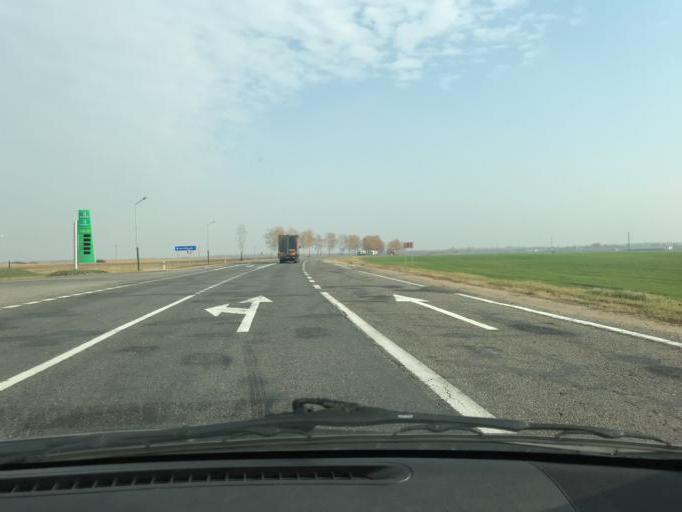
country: BY
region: Vitebsk
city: Chashniki
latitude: 55.0162
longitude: 29.1743
